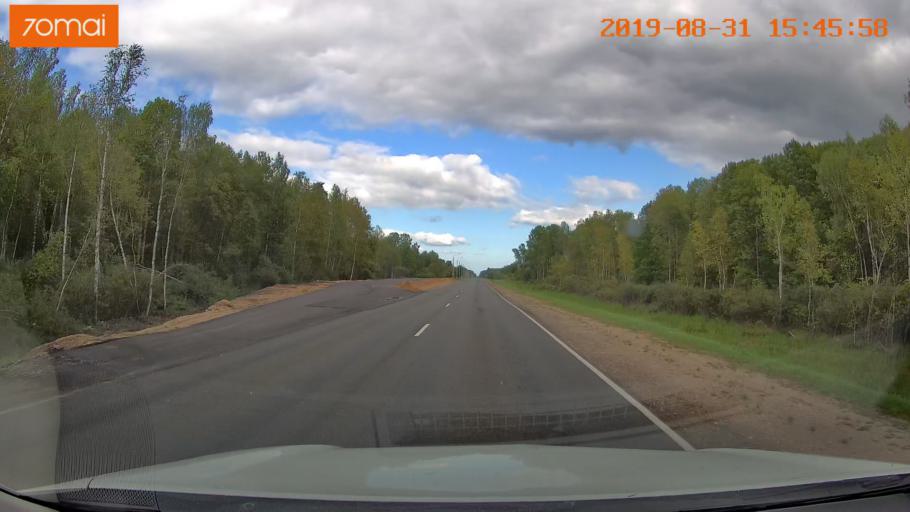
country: RU
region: Kaluga
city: Mosal'sk
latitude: 54.6699
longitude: 34.9727
